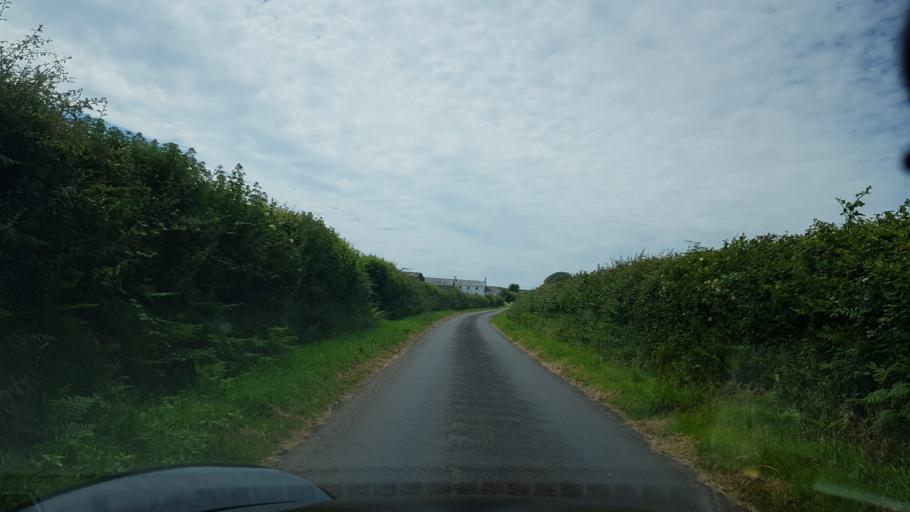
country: GB
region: Wales
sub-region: Carmarthenshire
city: Llanddowror
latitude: 51.7692
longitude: -4.4964
